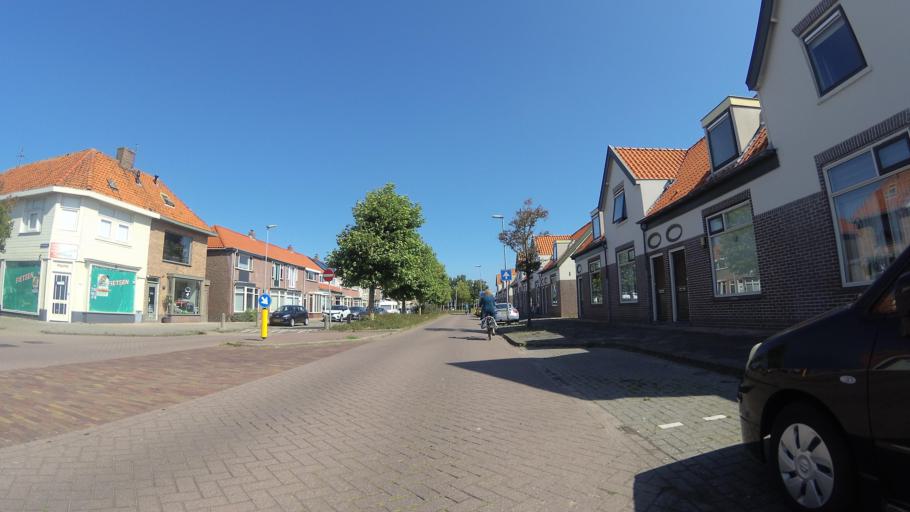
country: NL
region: North Holland
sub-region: Gemeente Den Helder
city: Den Helder
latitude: 52.9508
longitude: 4.7603
